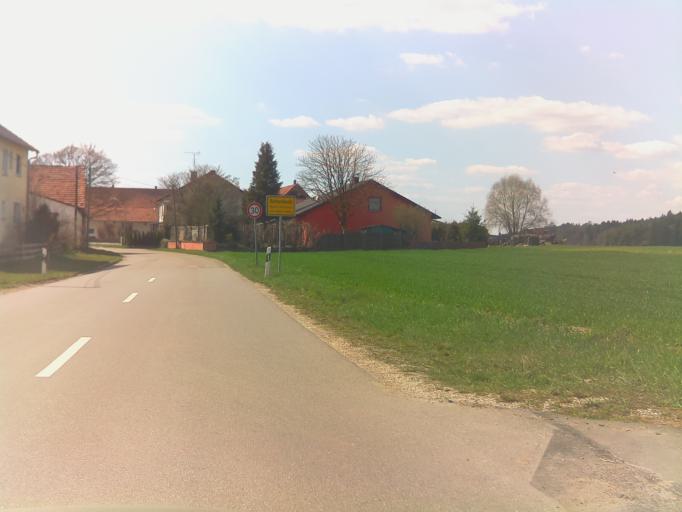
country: DE
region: Bavaria
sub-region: Swabia
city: Inchenhofen
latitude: 48.5377
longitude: 11.1556
